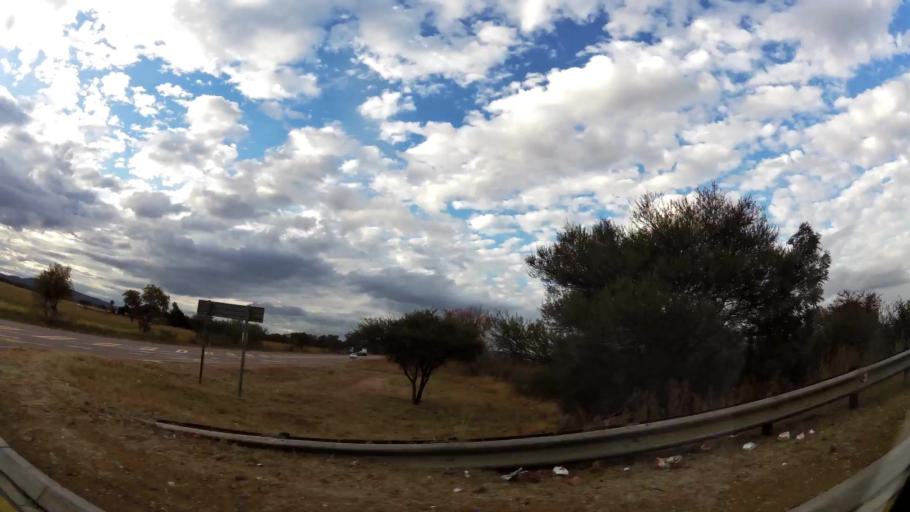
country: ZA
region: Limpopo
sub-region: Waterberg District Municipality
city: Modimolle
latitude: -24.5022
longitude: 28.7310
